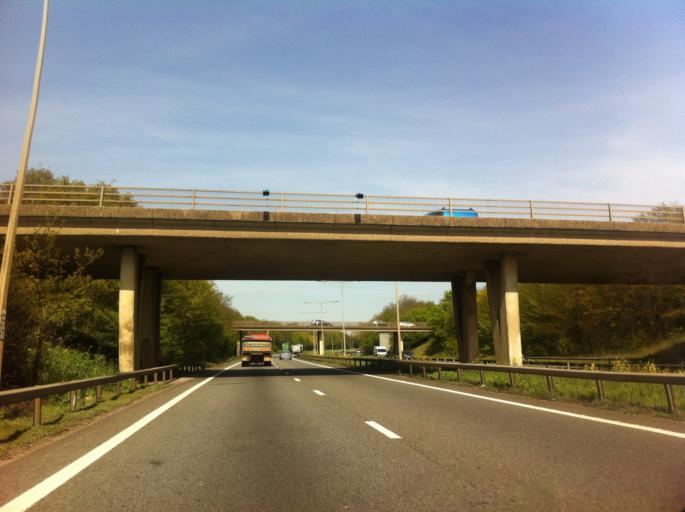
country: GB
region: England
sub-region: Northamptonshire
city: Northampton
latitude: 52.2446
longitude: -0.8377
